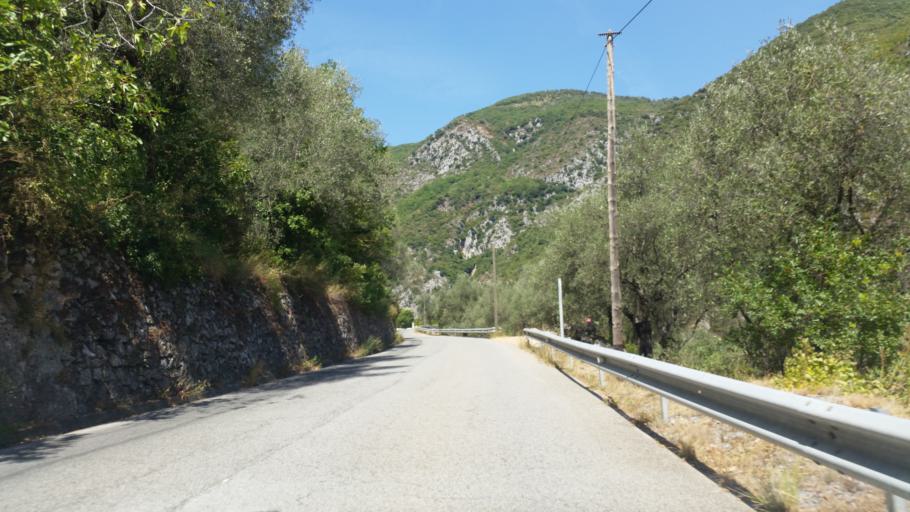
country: FR
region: Provence-Alpes-Cote d'Azur
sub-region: Departement des Alpes-Maritimes
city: Breil-sur-Roya
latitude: 43.9536
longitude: 7.5153
